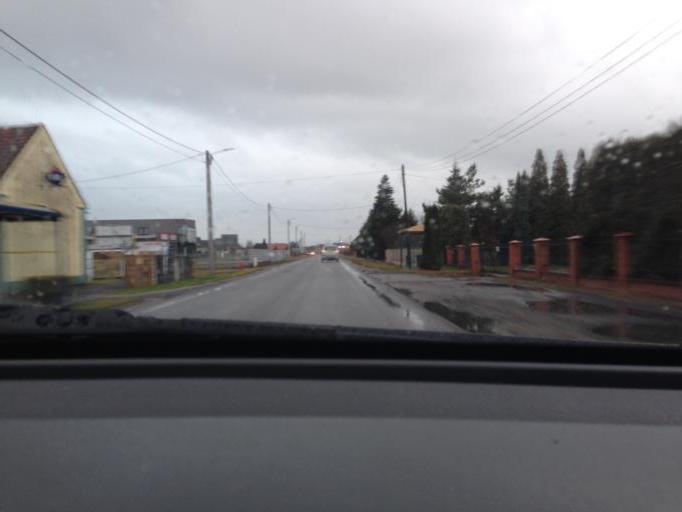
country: PL
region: Opole Voivodeship
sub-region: Powiat opolski
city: Wegry
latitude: 50.7203
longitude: 18.0092
